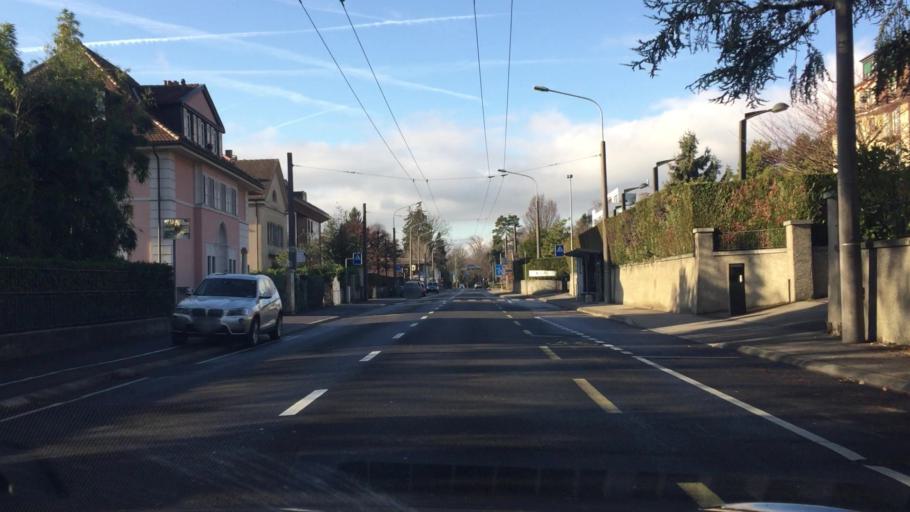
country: CH
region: Vaud
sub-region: Lavaux-Oron District
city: Pully
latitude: 46.5066
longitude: 6.6476
